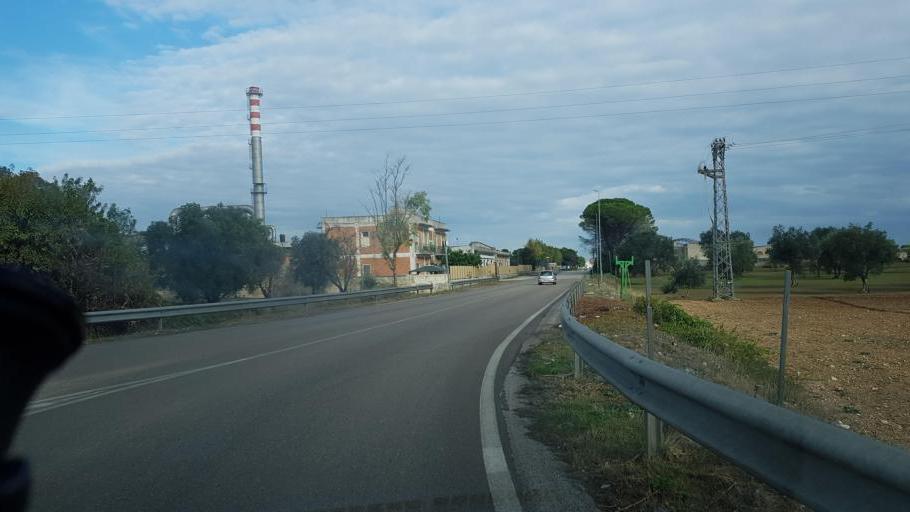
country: IT
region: Apulia
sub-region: Provincia di Brindisi
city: Francavilla Fontana
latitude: 40.5330
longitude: 17.5297
